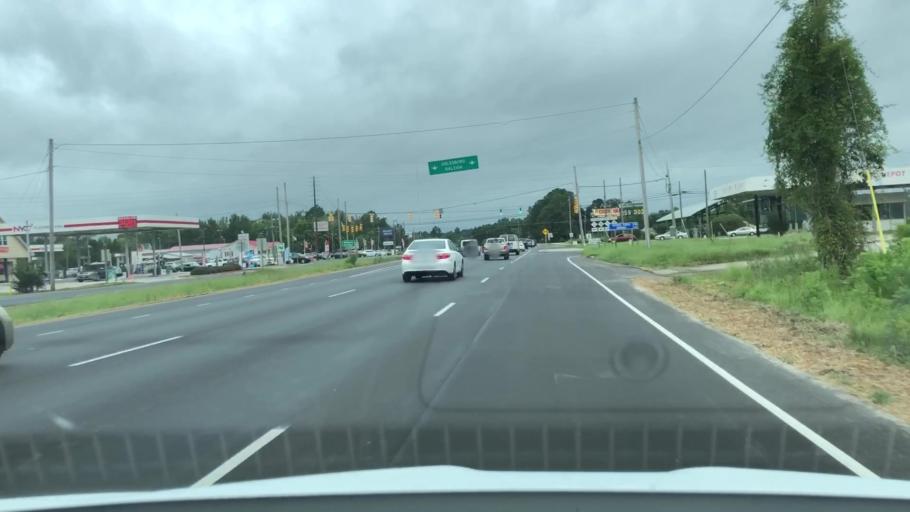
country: US
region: North Carolina
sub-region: Lenoir County
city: Kinston
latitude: 35.2537
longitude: -77.6006
